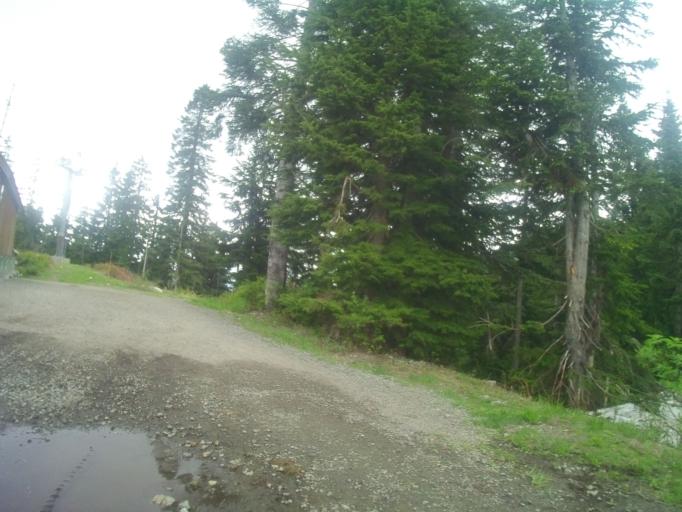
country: CA
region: British Columbia
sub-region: Fraser Valley Regional District
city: North Vancouver
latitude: 49.3831
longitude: -123.0787
